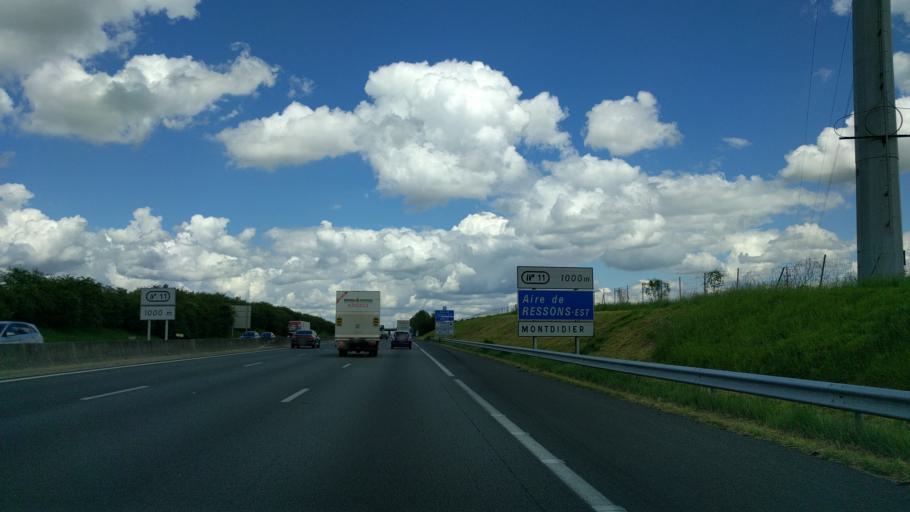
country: FR
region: Picardie
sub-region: Departement de l'Oise
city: Ressons-sur-Matz
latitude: 49.5081
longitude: 2.7185
